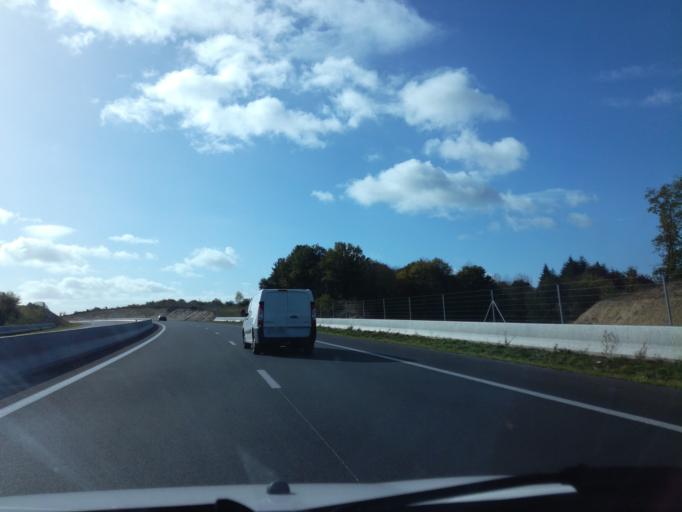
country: FR
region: Pays de la Loire
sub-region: Departement de Maine-et-Loire
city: Grez-Neuville
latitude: 47.6000
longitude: -0.7075
